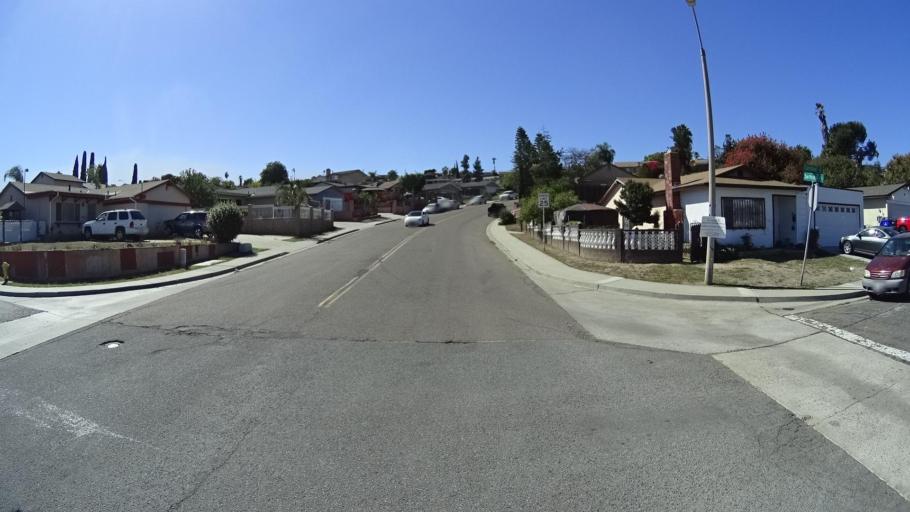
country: US
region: California
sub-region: San Diego County
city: La Presa
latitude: 32.7121
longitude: -117.0195
